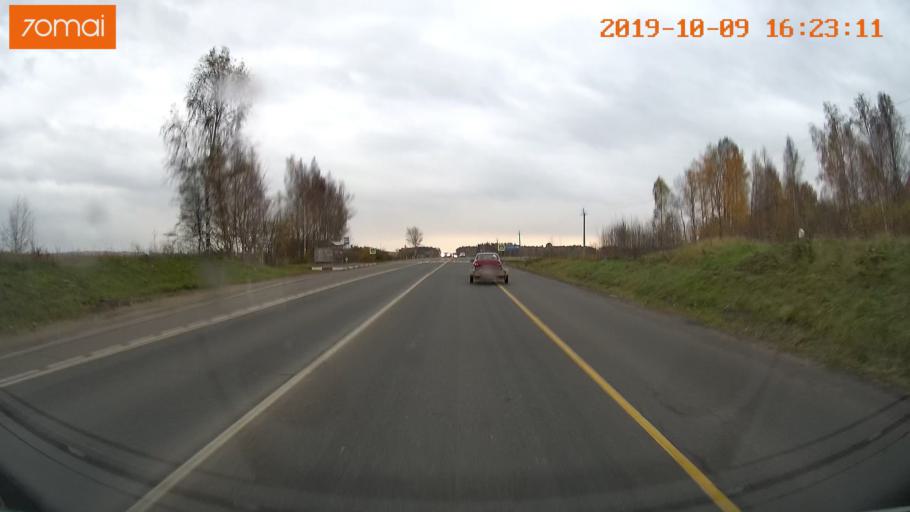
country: RU
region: Kostroma
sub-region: Kostromskoy Rayon
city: Kostroma
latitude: 57.6673
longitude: 40.8965
